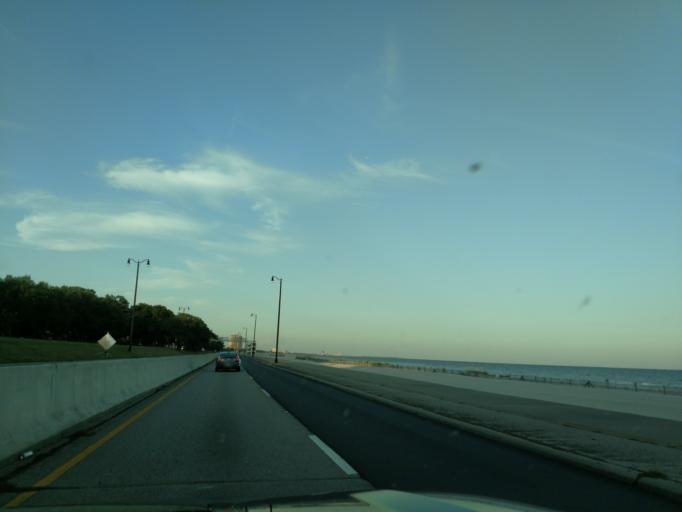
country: US
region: Mississippi
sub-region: Harrison County
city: Gulfport
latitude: 30.3838
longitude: -89.0203
